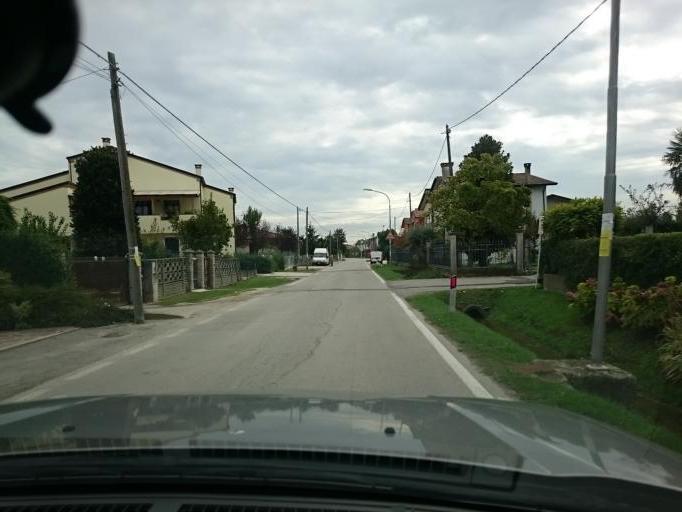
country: IT
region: Veneto
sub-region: Provincia di Padova
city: Arzergrande
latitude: 45.2837
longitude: 12.0624
